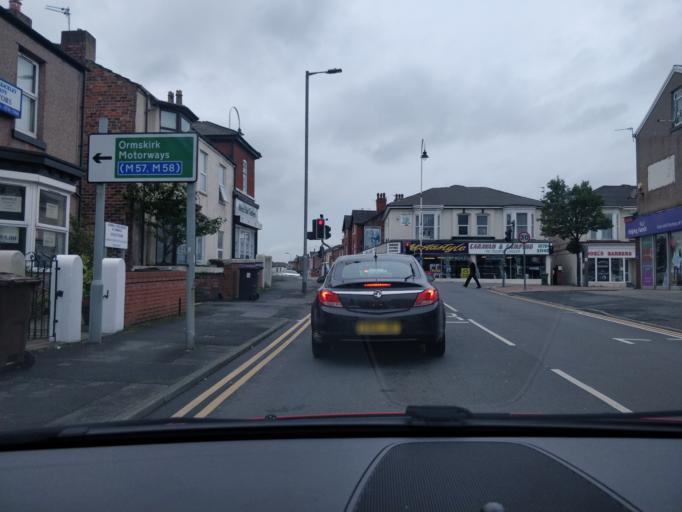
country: GB
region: England
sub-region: Sefton
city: Southport
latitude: 53.6435
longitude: -3.0020
